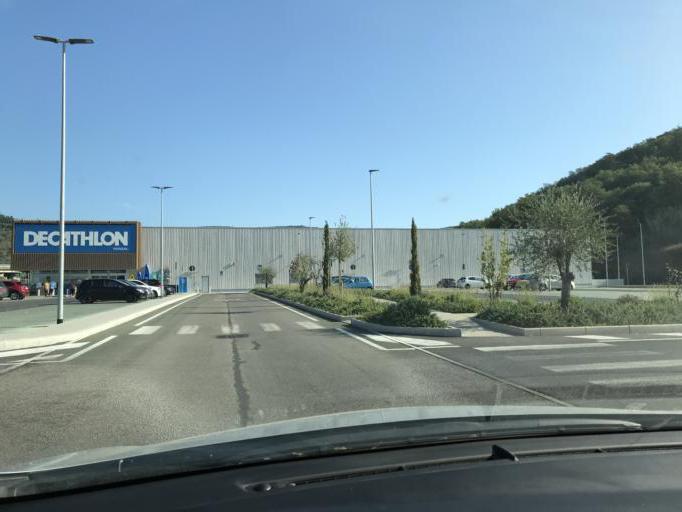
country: IT
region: Umbria
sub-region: Provincia di Perugia
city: Lacugnano
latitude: 43.1013
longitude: 12.3231
